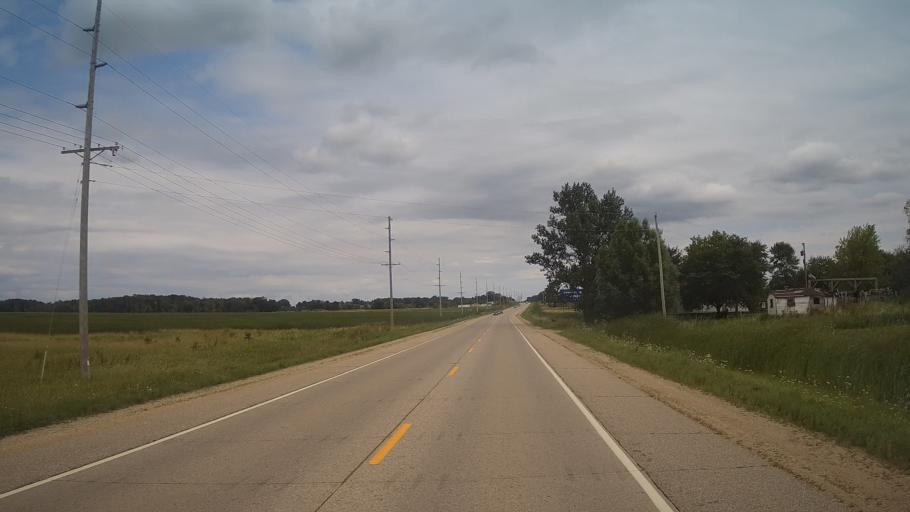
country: US
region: Wisconsin
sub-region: Waushara County
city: Redgranite
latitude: 44.0413
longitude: -89.0290
